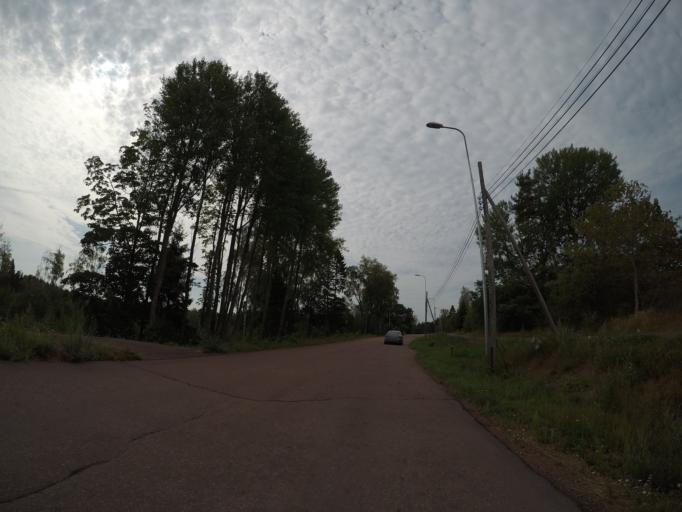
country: AX
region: Alands landsbygd
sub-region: Finstroem
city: Finstroem
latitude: 60.2197
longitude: 19.9806
